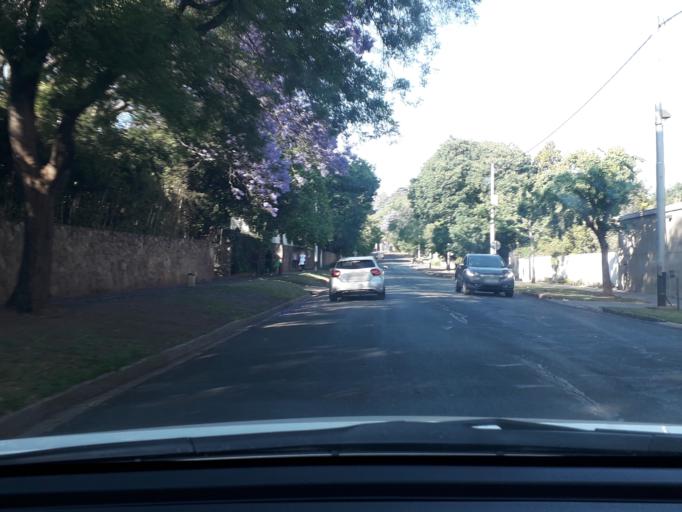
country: ZA
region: Gauteng
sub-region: City of Johannesburg Metropolitan Municipality
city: Johannesburg
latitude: -26.1698
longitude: 28.0222
